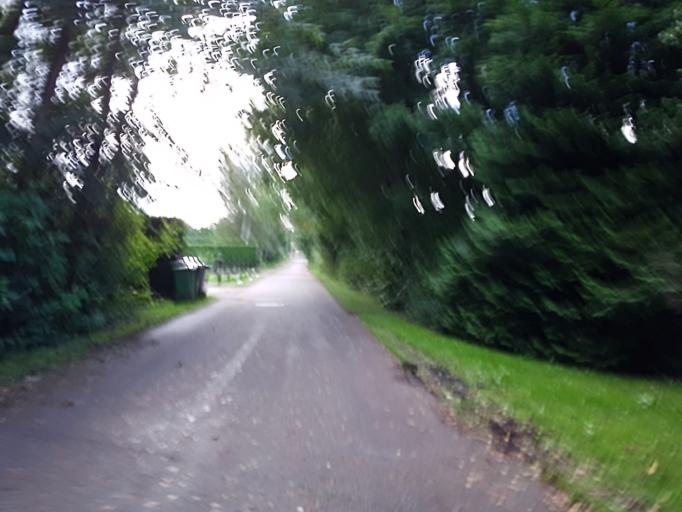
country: DK
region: Capital Region
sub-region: Egedal Kommune
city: Stenlose
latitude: 55.7382
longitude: 12.1975
